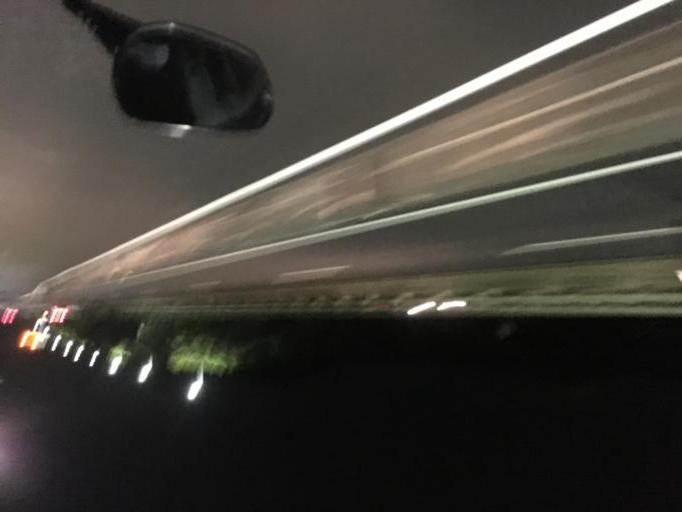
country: TW
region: Taiwan
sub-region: Hsinchu
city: Hsinchu
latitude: 24.7654
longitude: 120.9562
